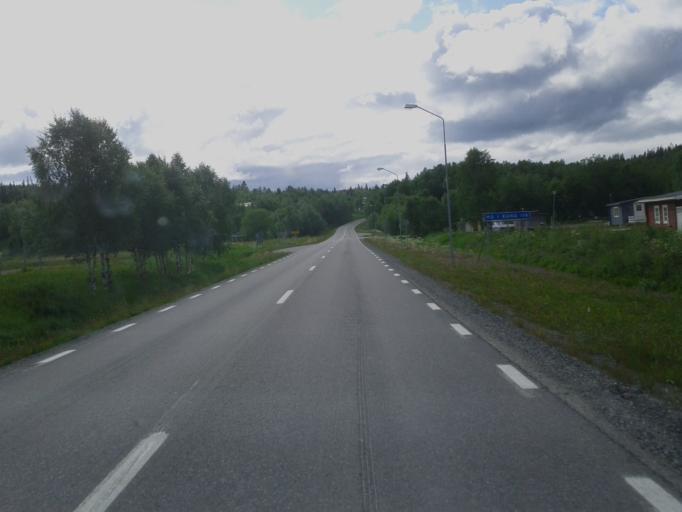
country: NO
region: Nordland
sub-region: Rana
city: Mo i Rana
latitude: 65.7105
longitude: 15.2440
